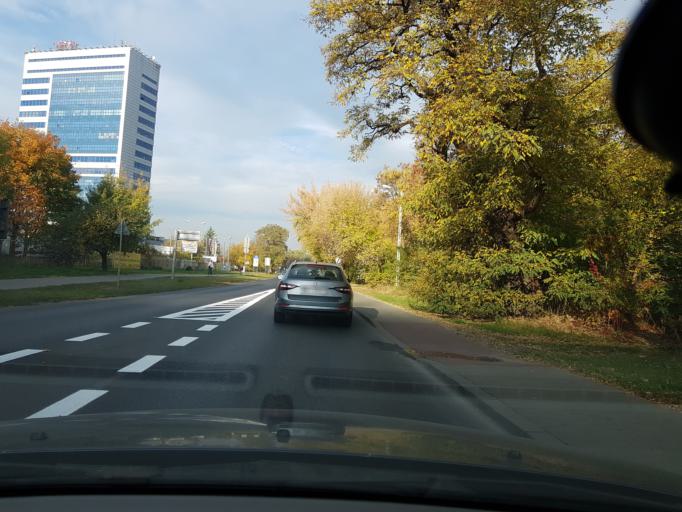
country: PL
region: Masovian Voivodeship
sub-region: Warszawa
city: Bielany
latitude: 52.2825
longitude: 20.9184
